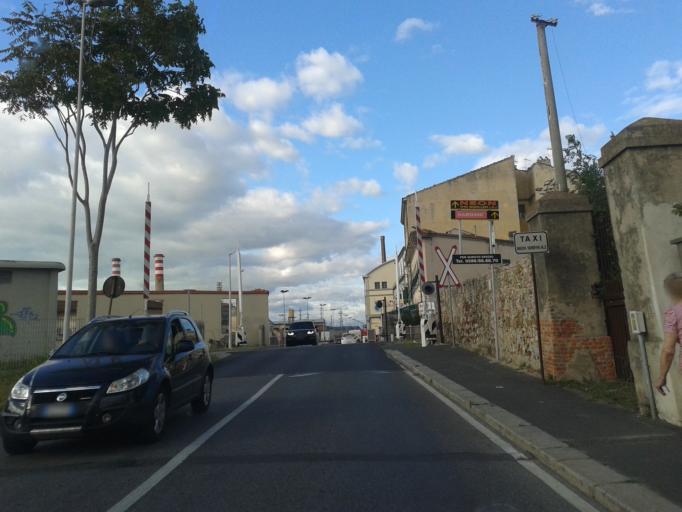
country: IT
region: Tuscany
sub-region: Provincia di Livorno
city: Livorno
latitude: 43.5618
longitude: 10.3124
